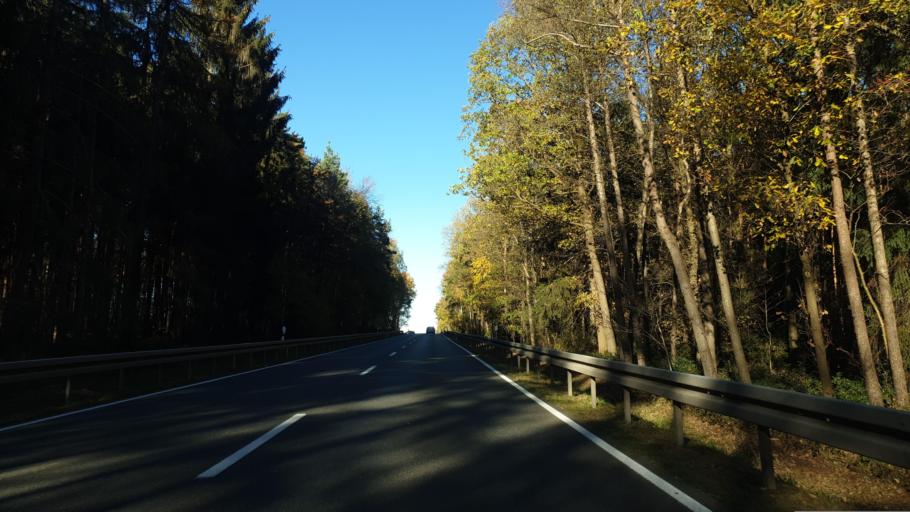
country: DE
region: Thuringia
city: Kuhdorf
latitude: 50.6965
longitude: 12.1168
